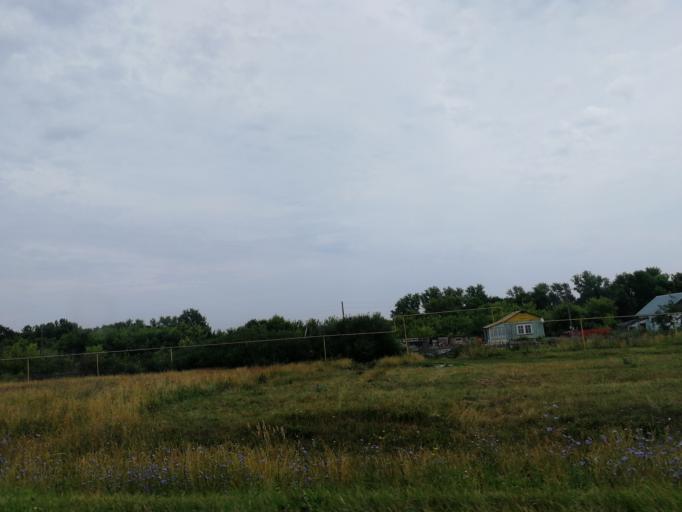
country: RU
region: Tula
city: Zhdankovskiy
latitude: 53.7139
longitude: 38.1382
